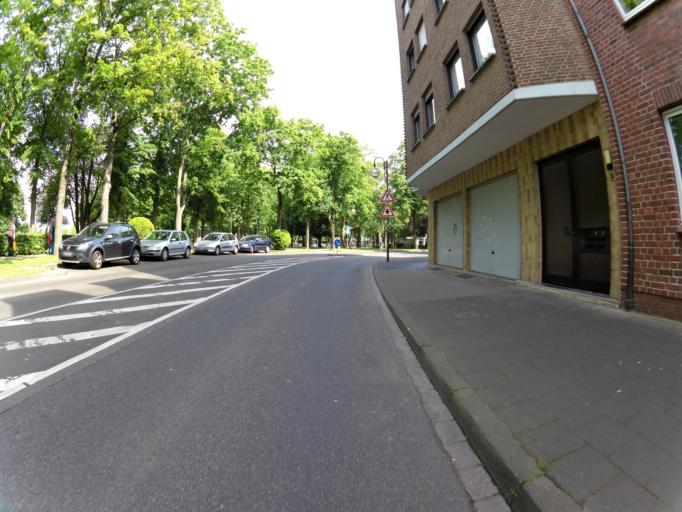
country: DE
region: North Rhine-Westphalia
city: Julich
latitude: 50.9235
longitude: 6.3594
